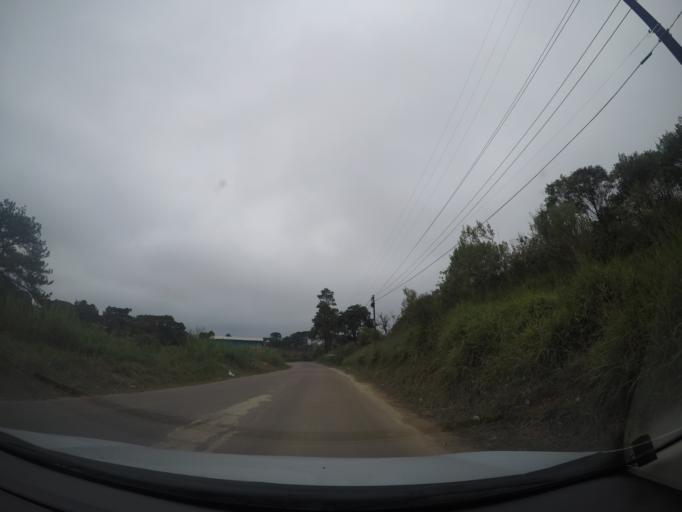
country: BR
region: Parana
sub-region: Colombo
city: Colombo
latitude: -25.3348
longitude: -49.2529
